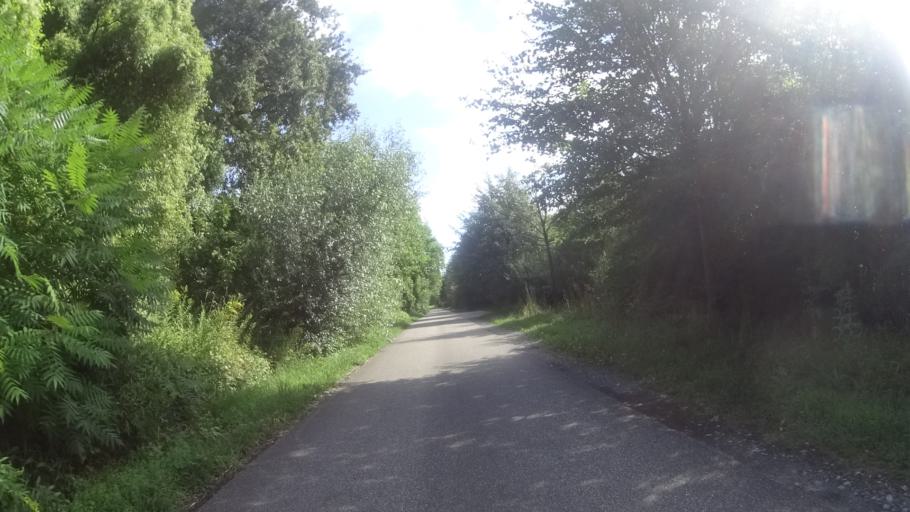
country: DE
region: Rheinland-Pfalz
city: Worth am Rhein
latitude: 49.0699
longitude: 8.2865
